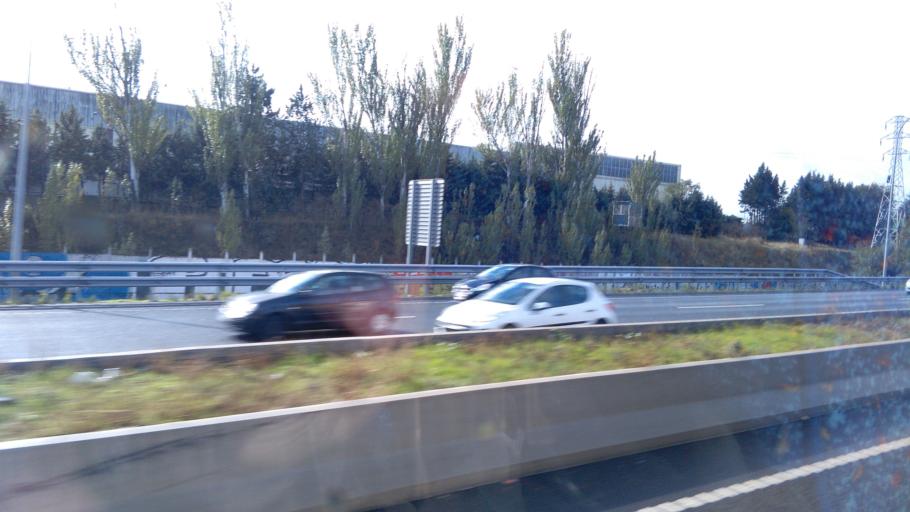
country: ES
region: Madrid
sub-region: Provincia de Madrid
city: Villaverde
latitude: 40.3640
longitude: -3.7078
